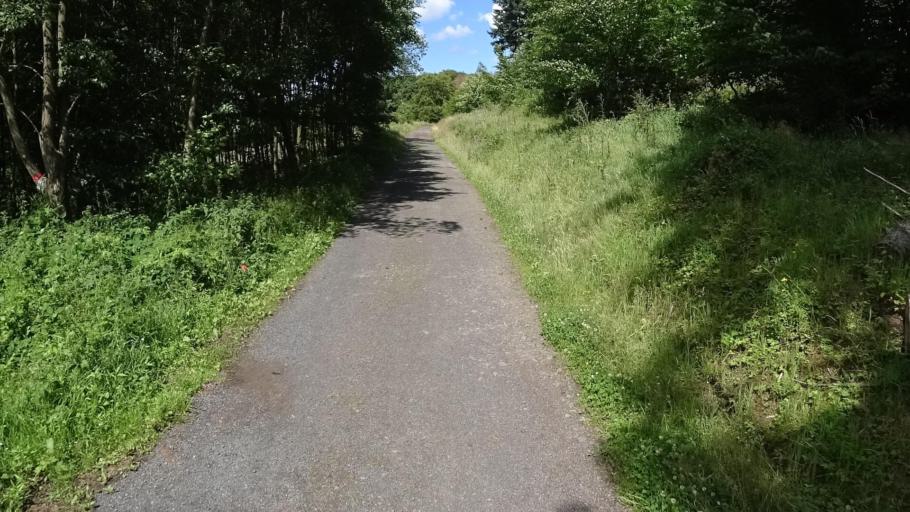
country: DE
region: Rheinland-Pfalz
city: Vettelschoss
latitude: 50.6137
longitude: 7.3261
